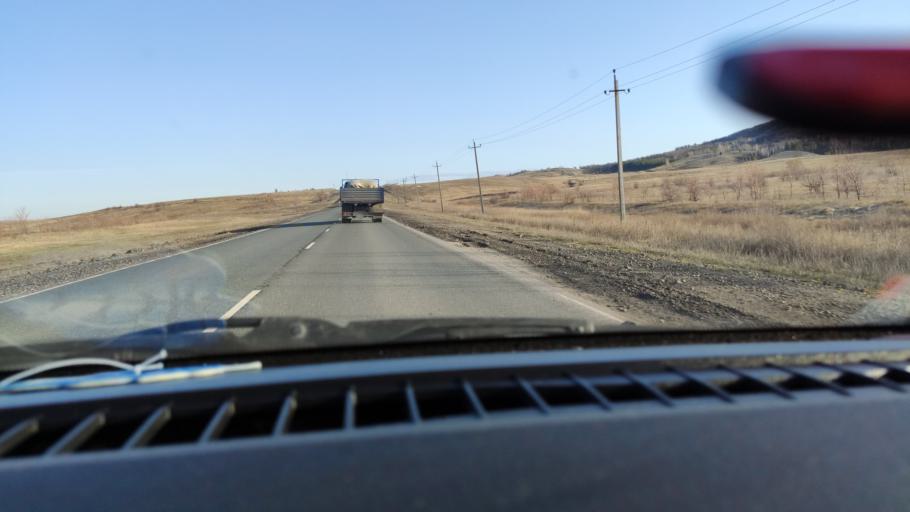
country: RU
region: Saratov
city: Alekseyevka
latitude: 52.3120
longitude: 47.9242
